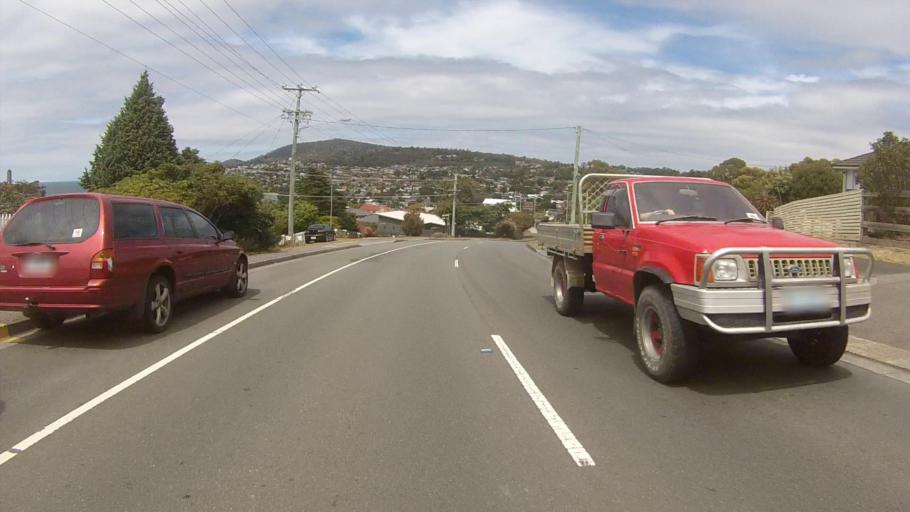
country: AU
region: Tasmania
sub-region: Kingborough
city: Blackmans Bay
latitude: -42.9950
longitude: 147.3239
